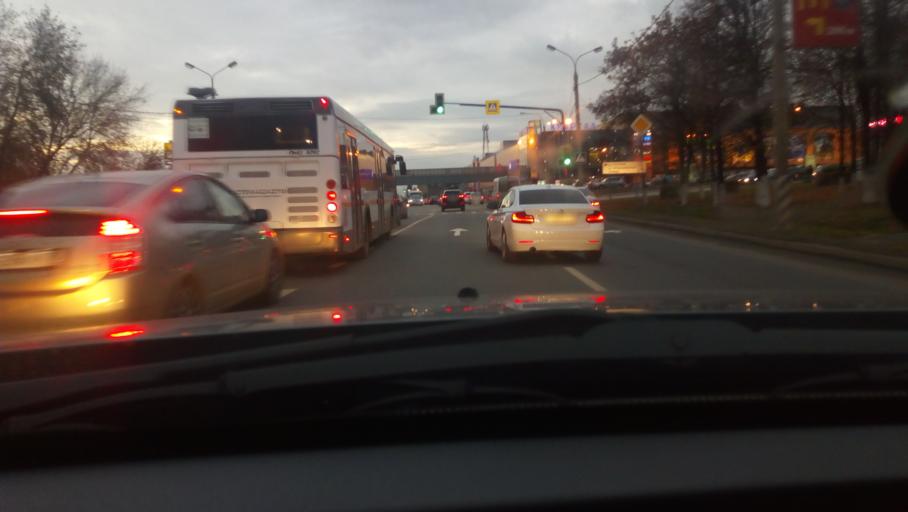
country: RU
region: Moskovskaya
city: Domodedovo
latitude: 55.4499
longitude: 37.7632
